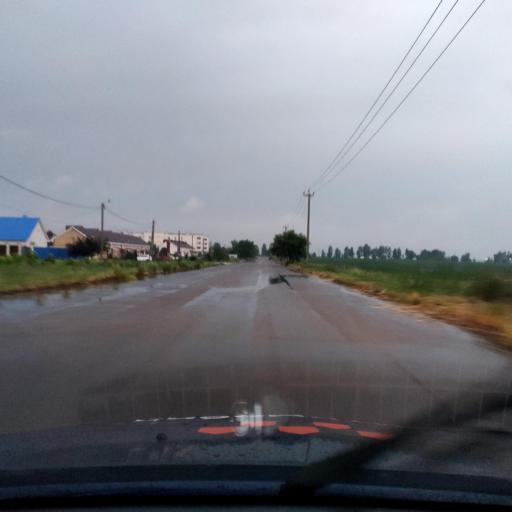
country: RU
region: Voronezj
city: Novaya Usman'
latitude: 51.6203
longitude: 39.3273
